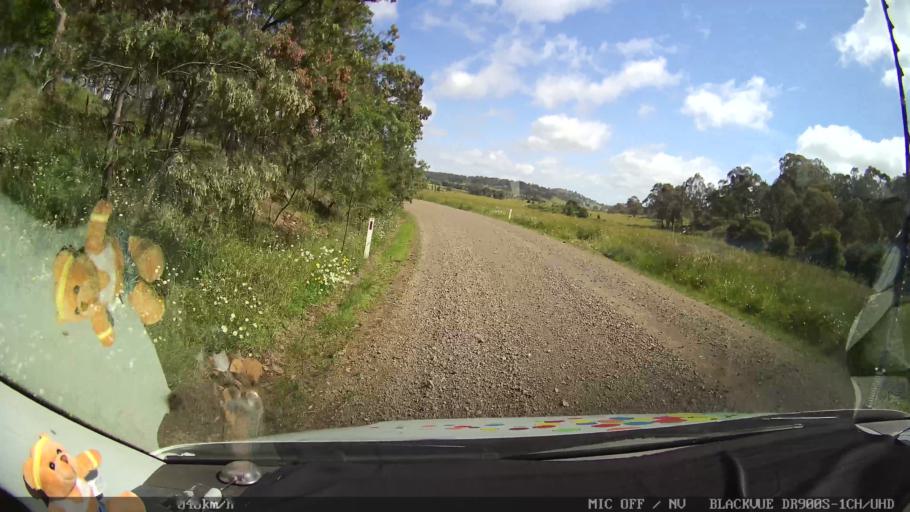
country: AU
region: New South Wales
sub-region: Guyra
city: Guyra
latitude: -29.9754
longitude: 151.6996
